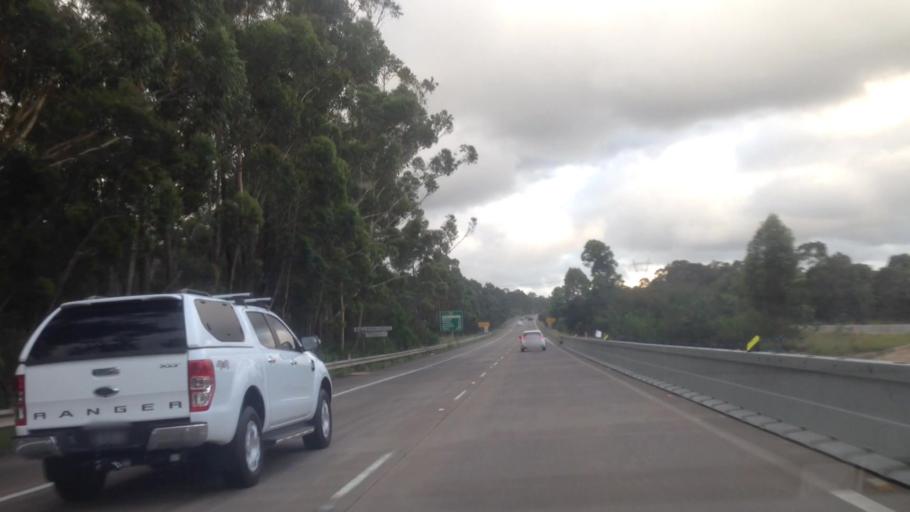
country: AU
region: New South Wales
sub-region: Wyong Shire
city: Jilliby
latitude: -33.2125
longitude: 151.4510
